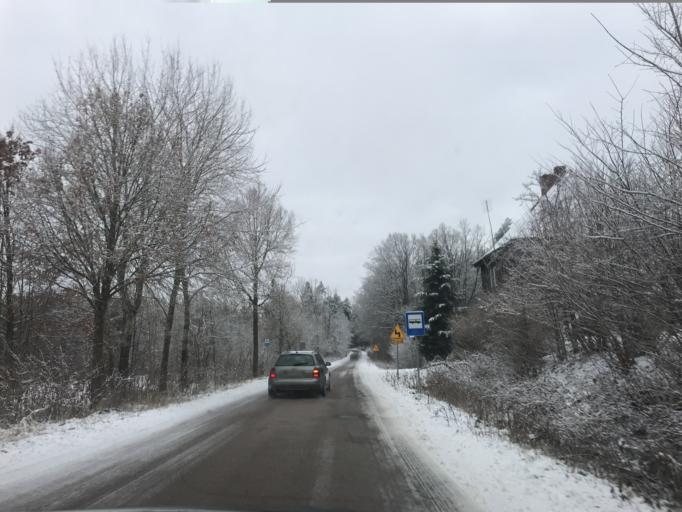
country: PL
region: Pomeranian Voivodeship
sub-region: Powiat bytowski
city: Parchowo
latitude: 54.2391
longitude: 17.5763
